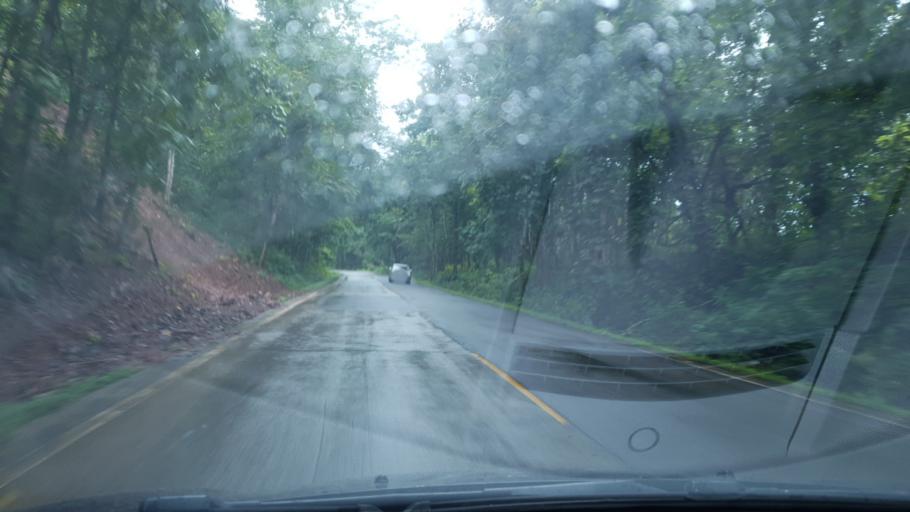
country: TH
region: Mae Hong Son
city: Pa Pae
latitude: 18.2543
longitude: 97.9421
